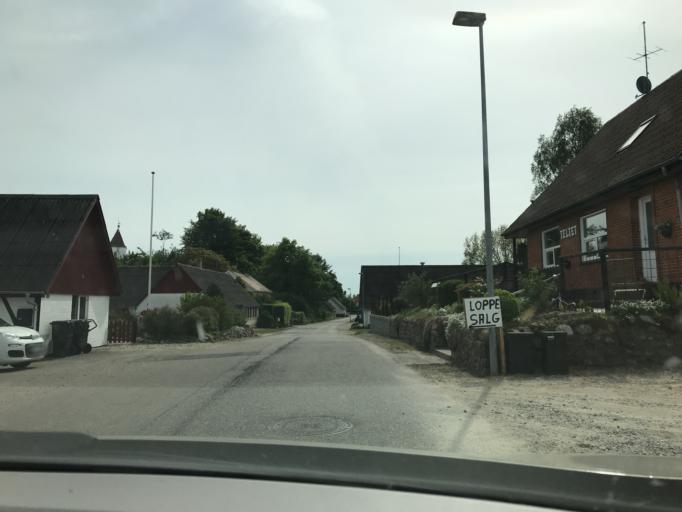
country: DK
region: Central Jutland
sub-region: Norddjurs Kommune
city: Allingabro
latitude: 56.5751
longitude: 10.2986
